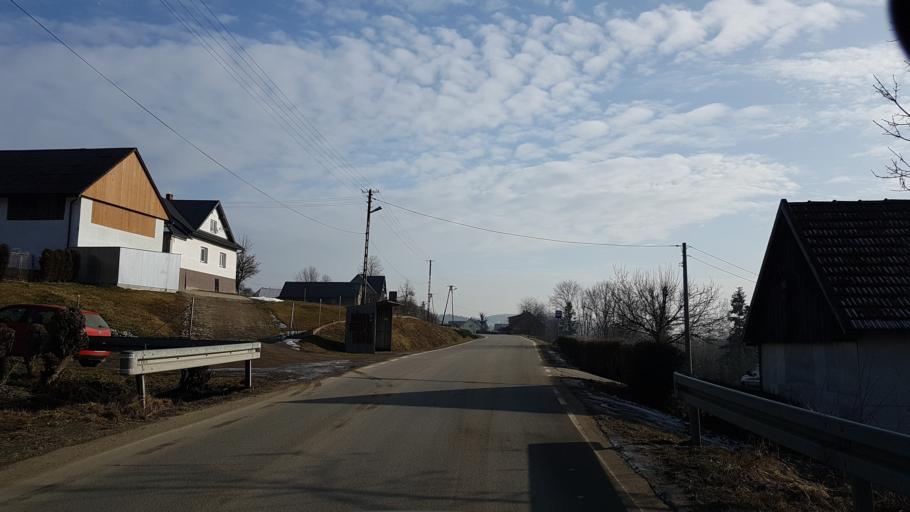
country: PL
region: Lesser Poland Voivodeship
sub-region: Powiat limanowski
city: Lukowica
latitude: 49.6319
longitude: 20.5373
